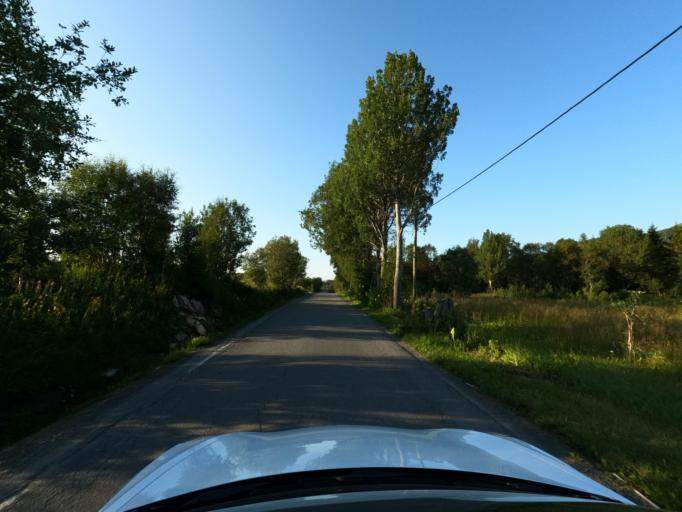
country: NO
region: Troms
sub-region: Skanland
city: Evenskjer
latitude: 68.4696
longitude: 16.7027
